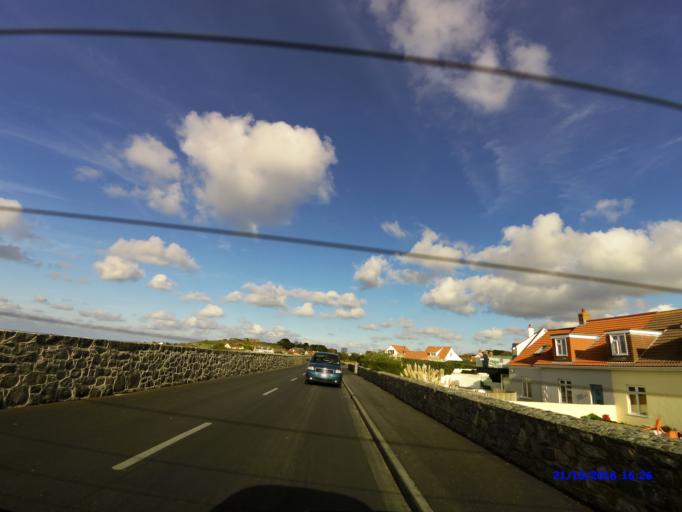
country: GG
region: St Peter Port
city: Saint Peter Port
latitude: 49.4605
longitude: -2.6331
